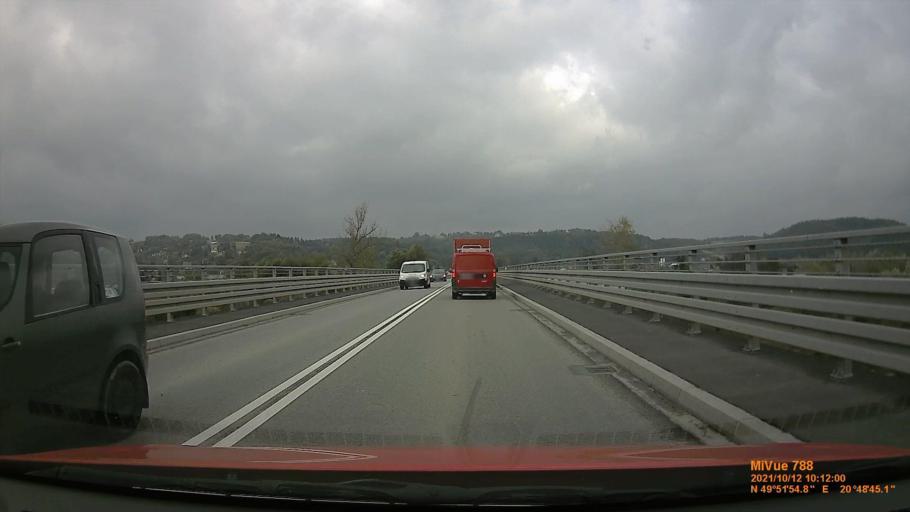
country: PL
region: Lesser Poland Voivodeship
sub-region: Powiat tarnowski
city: Zakliczyn
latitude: 49.8631
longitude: 20.8054
